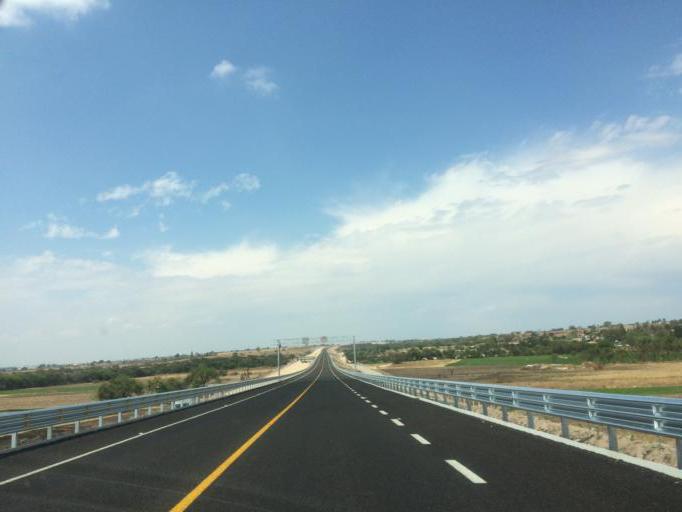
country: MX
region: Guanajuato
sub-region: Silao de la Victoria
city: San Francisco (Banos de Agua Caliente)
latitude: 21.0343
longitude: -101.4849
